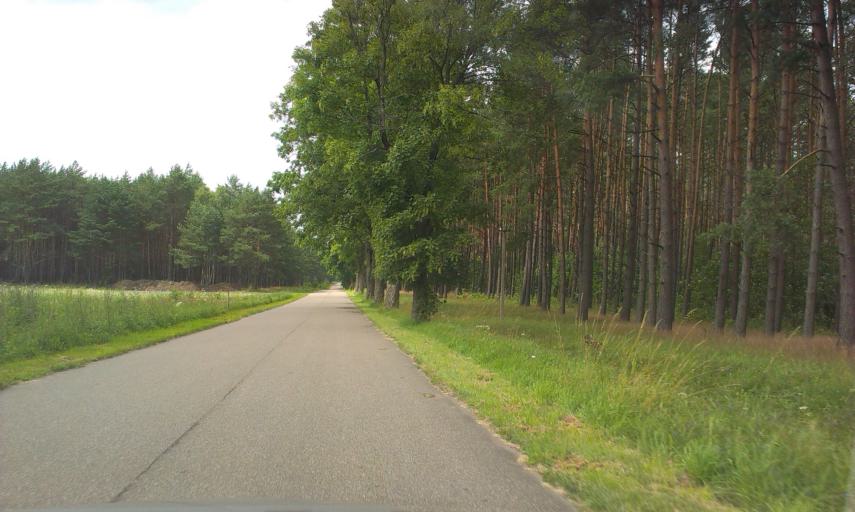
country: PL
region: West Pomeranian Voivodeship
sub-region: Powiat szczecinecki
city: Lubowo
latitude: 53.6409
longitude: 16.3252
